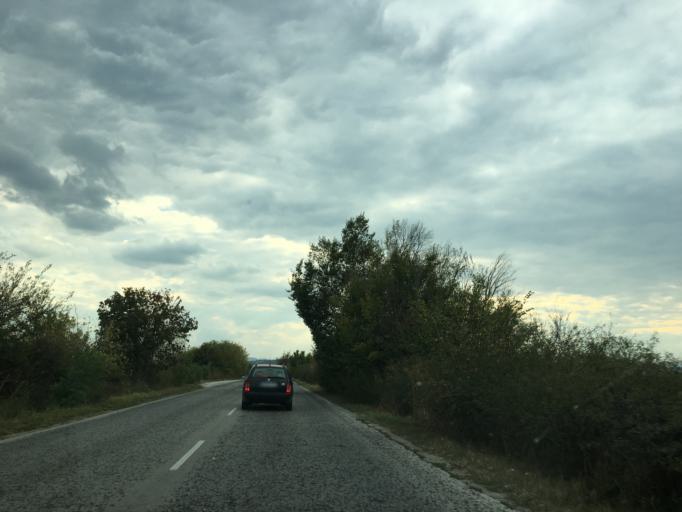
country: BG
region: Vratsa
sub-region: Obshtina Borovan
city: Borovan
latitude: 43.3650
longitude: 23.6982
